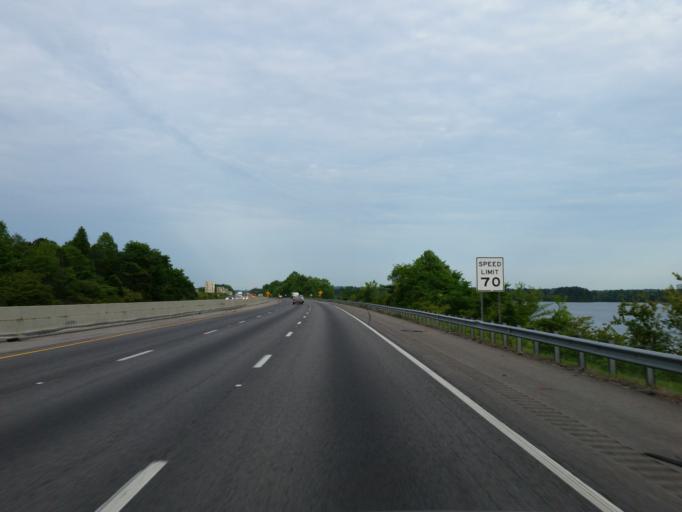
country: US
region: Alabama
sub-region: Saint Clair County
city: Riverside
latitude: 33.5960
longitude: -86.2047
